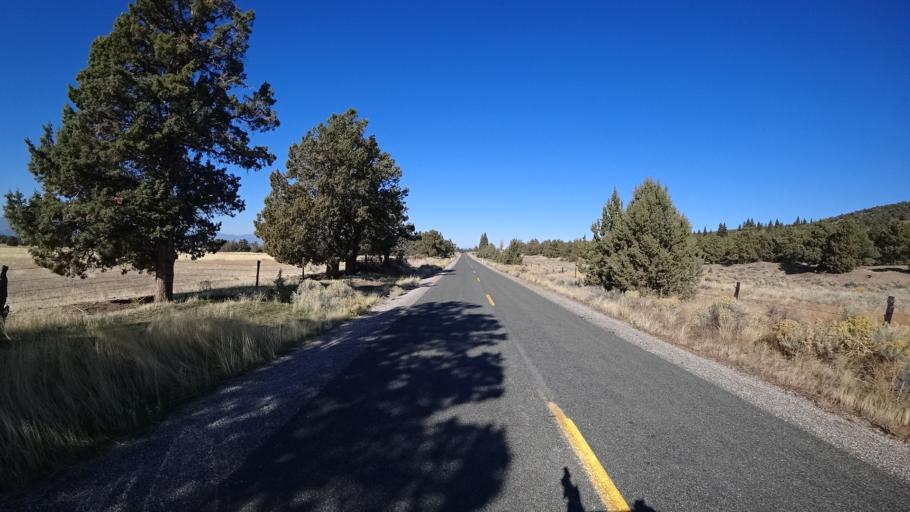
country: US
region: California
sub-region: Siskiyou County
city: Weed
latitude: 41.6189
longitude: -122.3214
